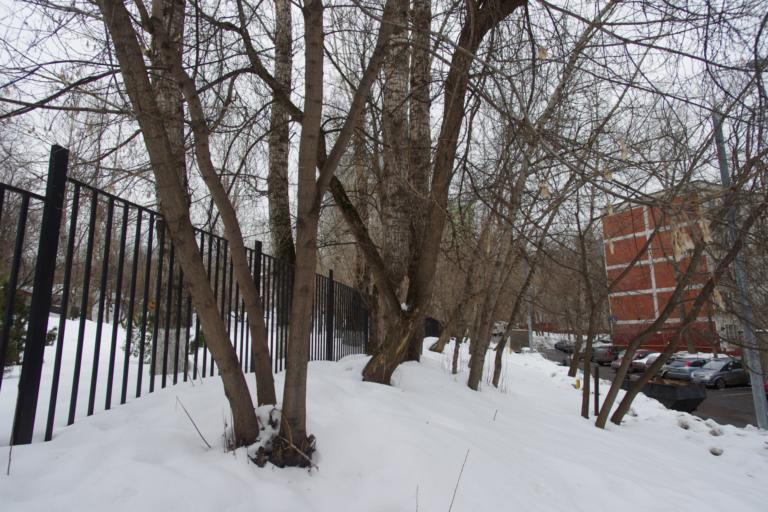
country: RU
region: Moskovskaya
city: Khoroshevo-Mnevniki
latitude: 55.7695
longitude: 37.4727
